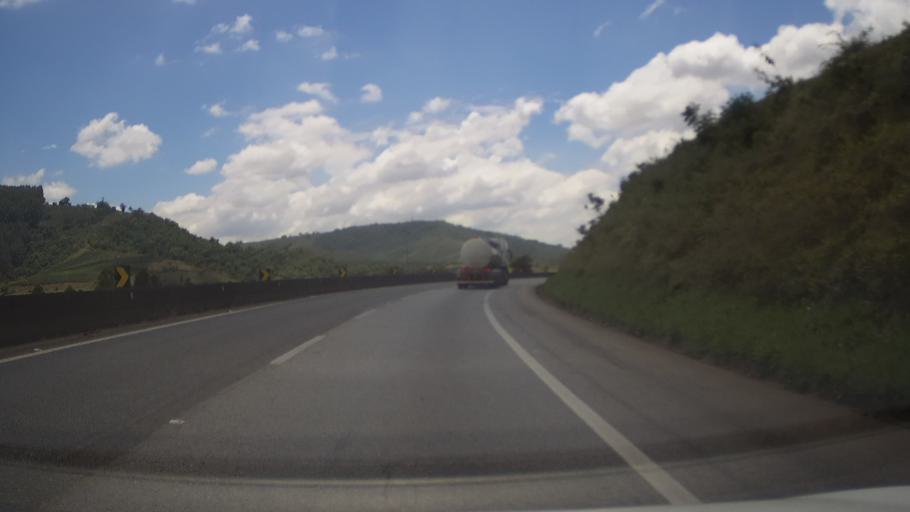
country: BR
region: Minas Gerais
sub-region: Campanha
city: Campanha
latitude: -21.8108
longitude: -45.4886
